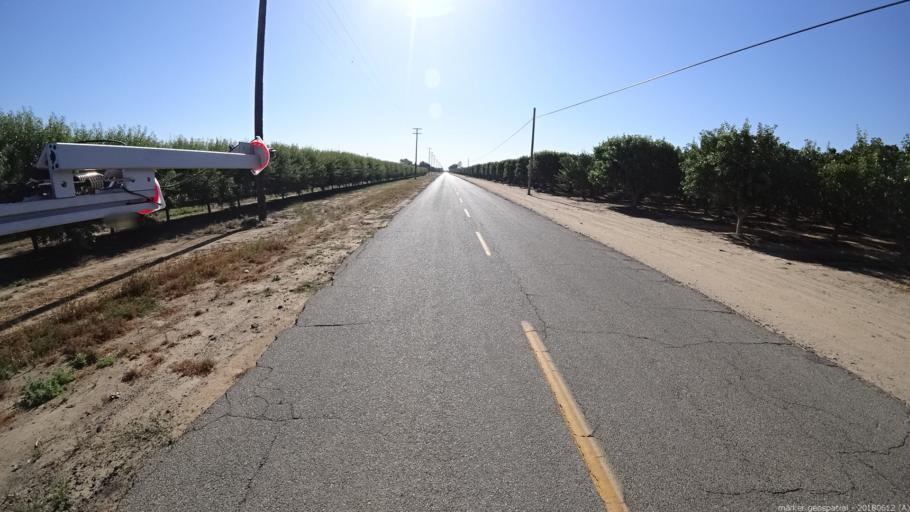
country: US
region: California
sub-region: Madera County
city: Madera Acres
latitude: 37.0110
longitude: -120.1447
